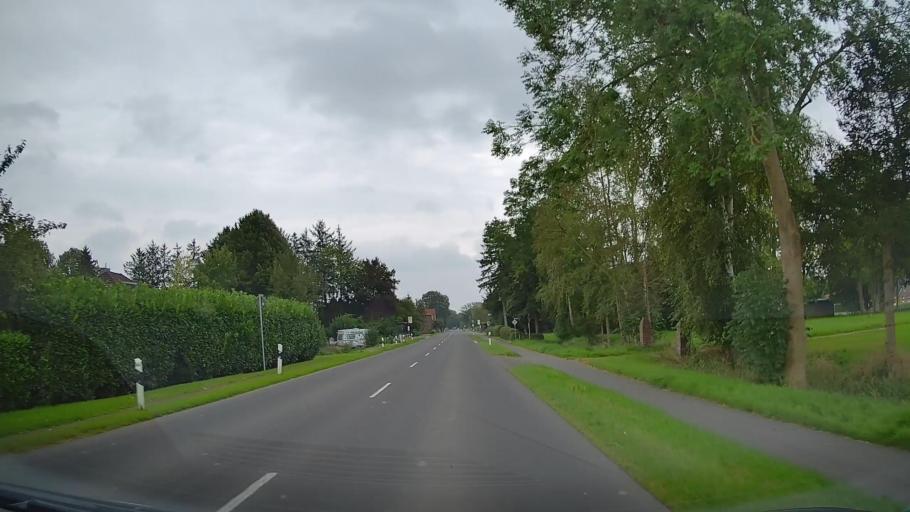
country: DE
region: Lower Saxony
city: Drochtersen
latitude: 53.7217
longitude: 9.3619
